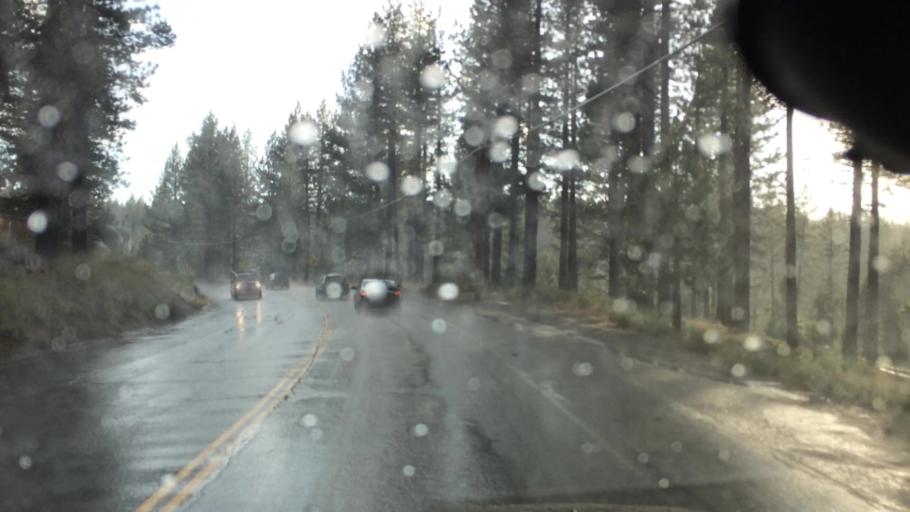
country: US
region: California
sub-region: El Dorado County
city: South Lake Tahoe
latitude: 38.9055
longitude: -119.9674
